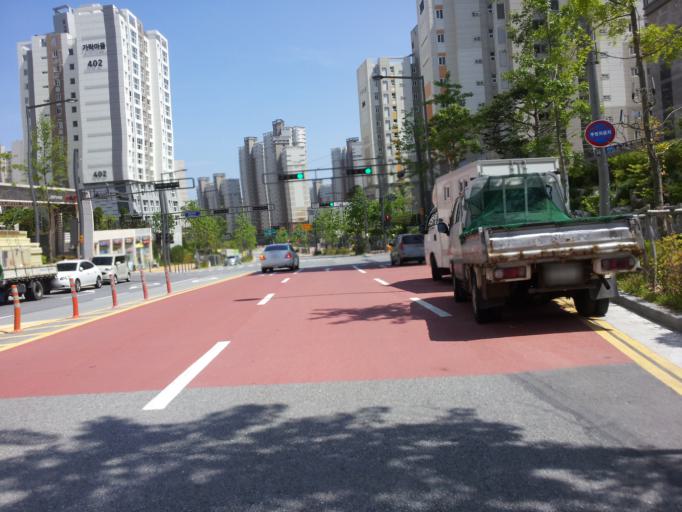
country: KR
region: Chungcheongnam-do
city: Gongju
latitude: 36.5072
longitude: 127.2360
